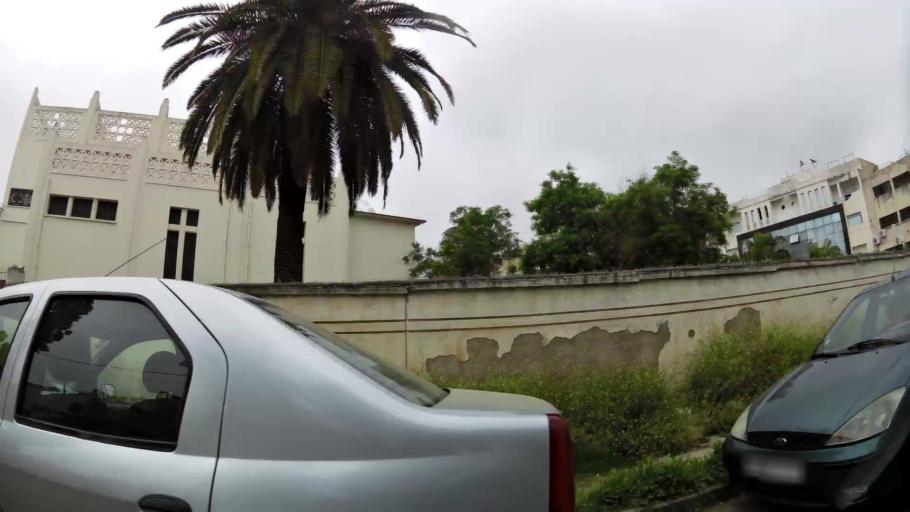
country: MA
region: Fes-Boulemane
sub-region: Fes
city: Fes
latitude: 34.0380
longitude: -4.9941
